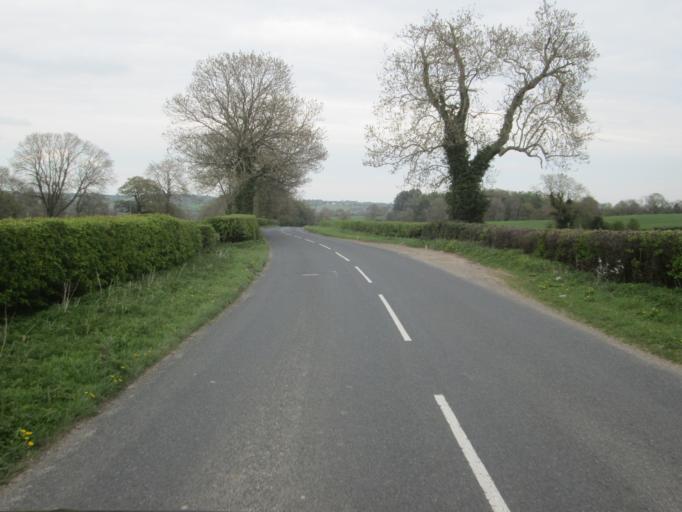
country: GB
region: England
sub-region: Derbyshire
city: Yeldersley
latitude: 52.9765
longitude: -1.6192
